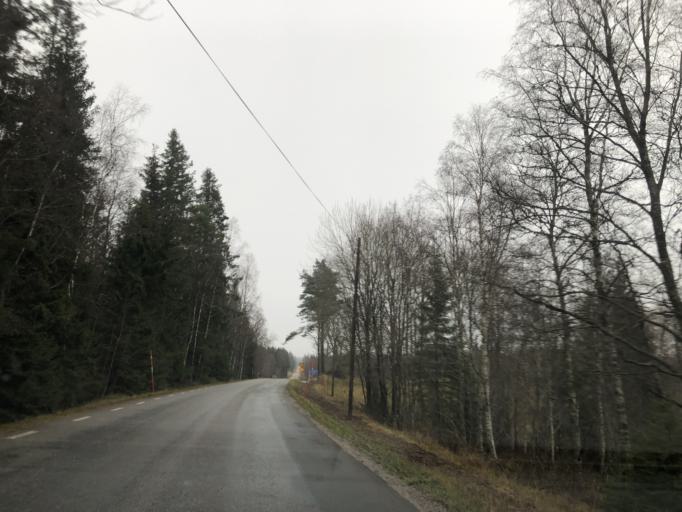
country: SE
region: Vaestra Goetaland
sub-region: Ulricehamns Kommun
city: Ulricehamn
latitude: 57.7239
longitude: 13.5462
